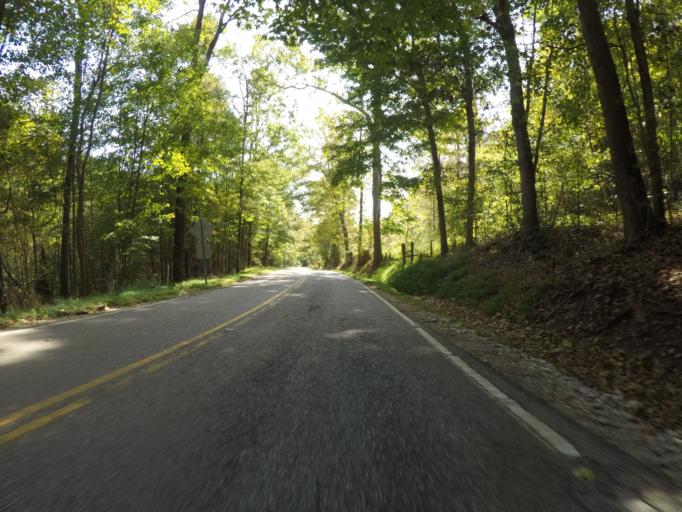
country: US
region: West Virginia
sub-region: Cabell County
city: Lesage
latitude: 38.5838
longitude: -82.4220
